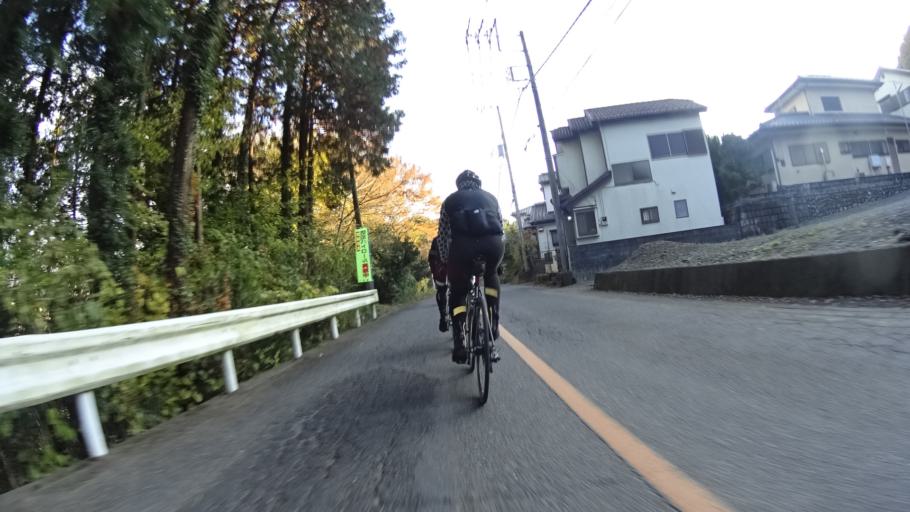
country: JP
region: Saitama
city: Hanno
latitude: 35.8503
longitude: 139.3130
